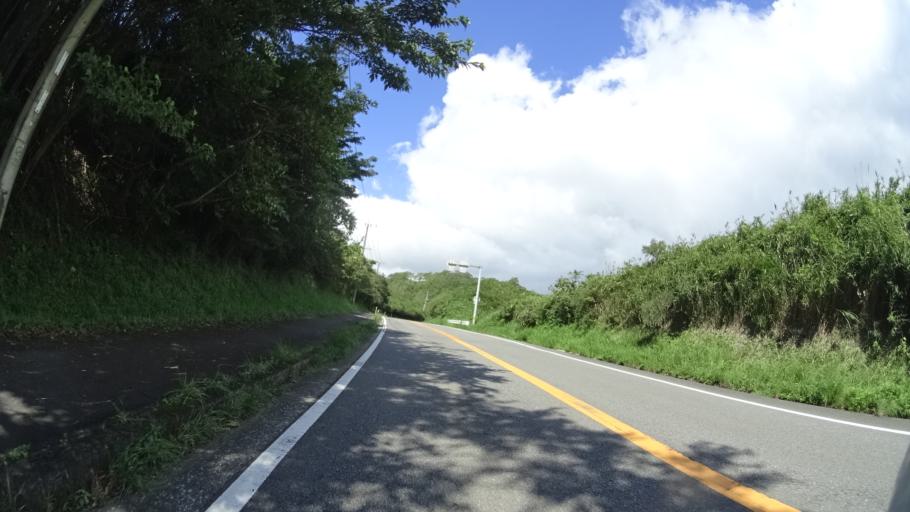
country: JP
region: Oita
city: Beppu
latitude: 33.3414
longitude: 131.4577
